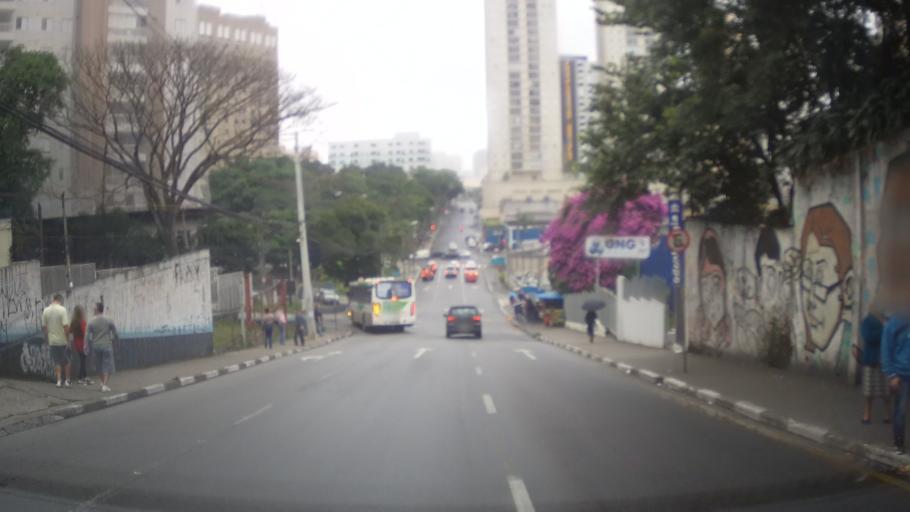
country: BR
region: Sao Paulo
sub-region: Guarulhos
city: Guarulhos
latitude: -23.4711
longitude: -46.5314
